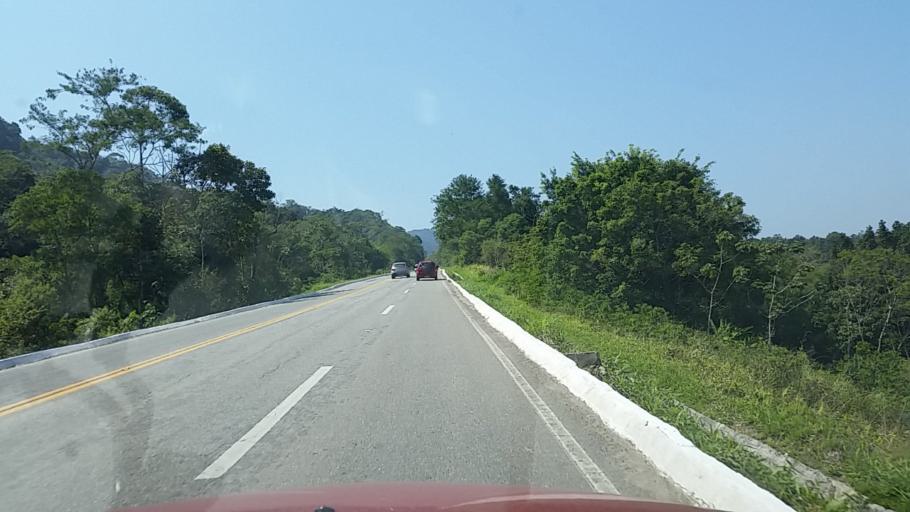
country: BR
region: Sao Paulo
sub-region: Miracatu
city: Miracatu
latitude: -24.3801
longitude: -47.5156
